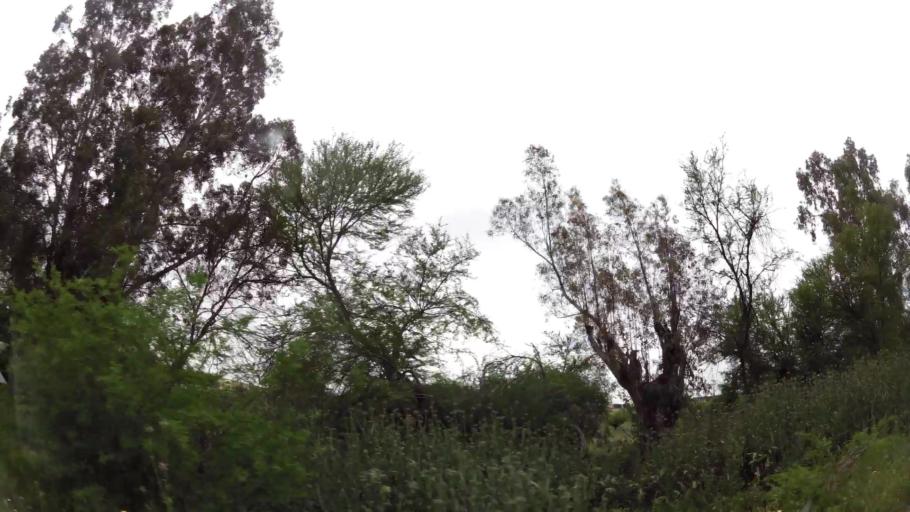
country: MA
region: Rabat-Sale-Zemmour-Zaer
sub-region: Khemisset
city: Tiflet
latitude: 33.8429
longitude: -6.2704
